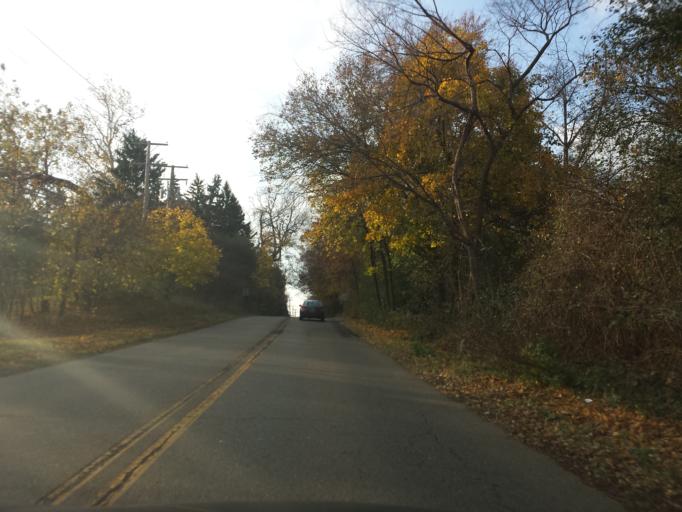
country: US
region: Michigan
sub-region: Oakland County
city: Bloomfield Hills
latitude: 42.5901
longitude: -83.2473
